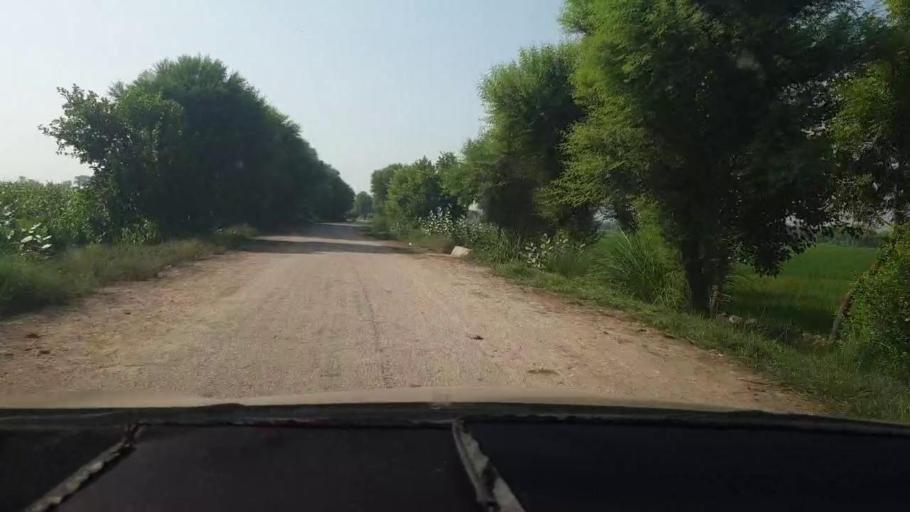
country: PK
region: Sindh
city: Kambar
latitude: 27.6164
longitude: 68.0906
